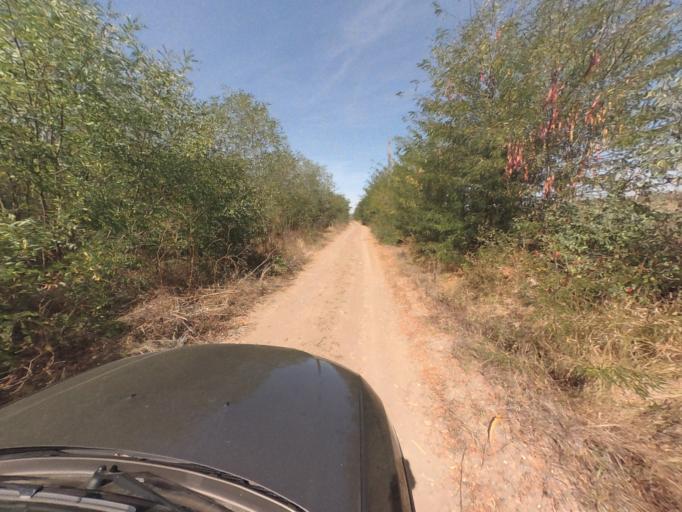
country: RO
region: Vaslui
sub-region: Comuna Costesti
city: Costesti
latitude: 46.5209
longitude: 27.7397
